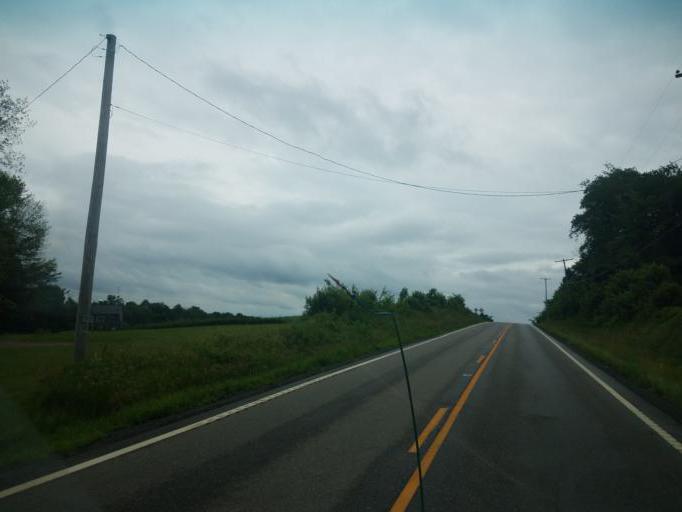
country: US
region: Ohio
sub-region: Columbiana County
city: Lisbon
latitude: 40.7701
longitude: -80.8398
